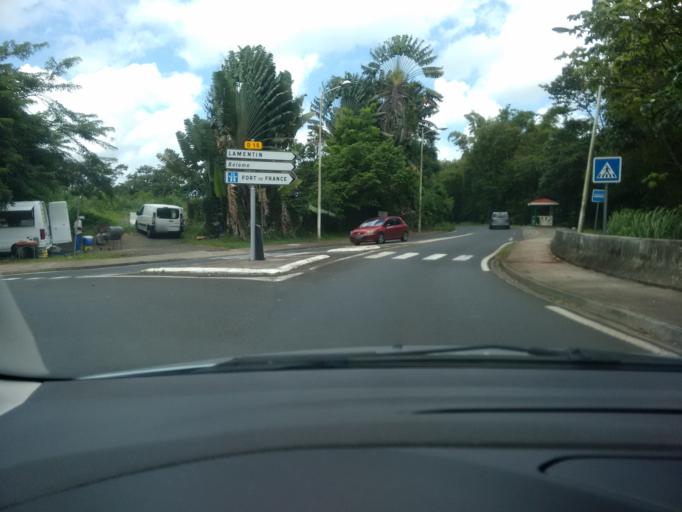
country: MQ
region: Martinique
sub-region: Martinique
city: Saint-Joseph
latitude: 14.6716
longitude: -61.0229
